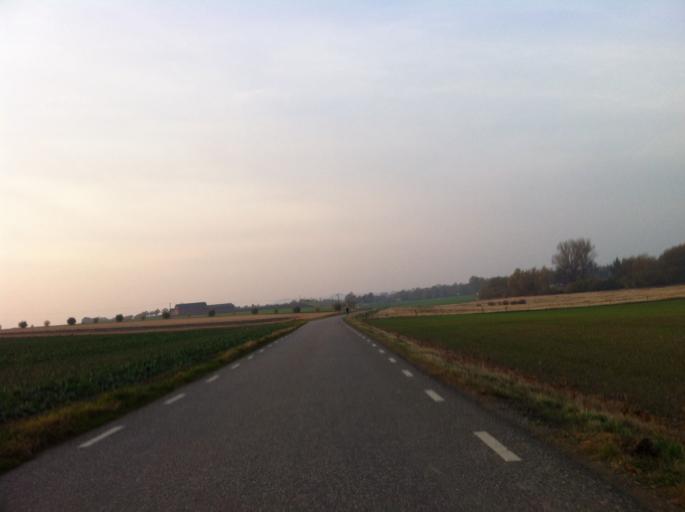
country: SE
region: Skane
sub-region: Svalovs Kommun
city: Teckomatorp
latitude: 55.8707
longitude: 13.0158
